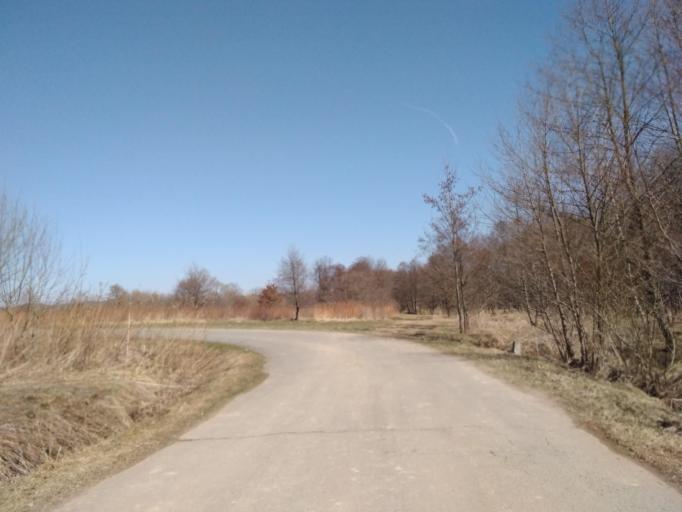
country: PL
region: Subcarpathian Voivodeship
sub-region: Powiat brzozowski
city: Orzechowka
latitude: 49.7109
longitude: 21.9685
